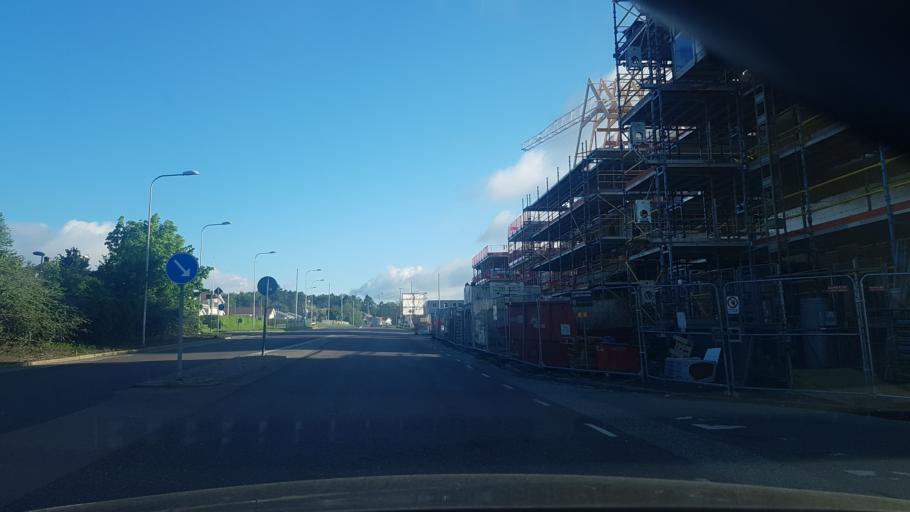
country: SE
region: Vaestra Goetaland
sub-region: Goteborg
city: Majorna
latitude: 57.6407
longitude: 11.8811
